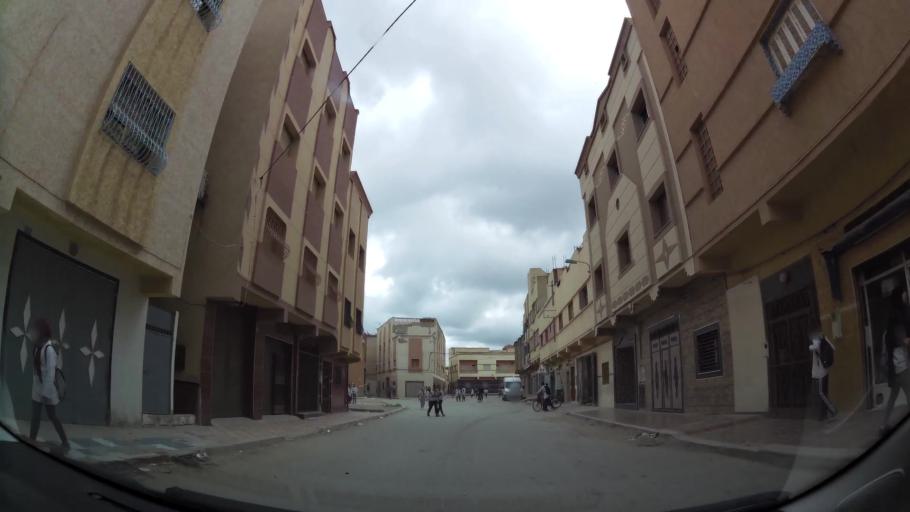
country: MA
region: Oriental
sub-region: Nador
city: Nador
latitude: 35.1682
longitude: -2.9388
